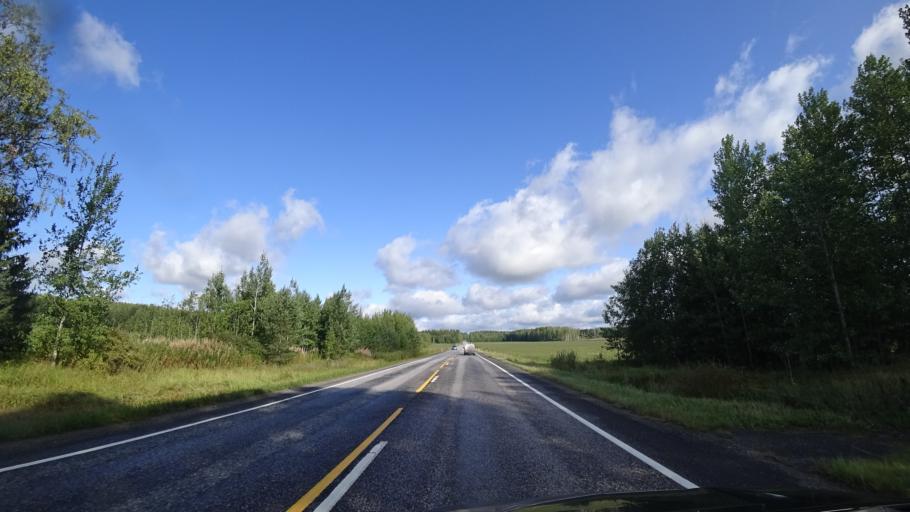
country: FI
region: Uusimaa
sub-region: Helsinki
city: Tuusula
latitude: 60.4662
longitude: 24.9453
